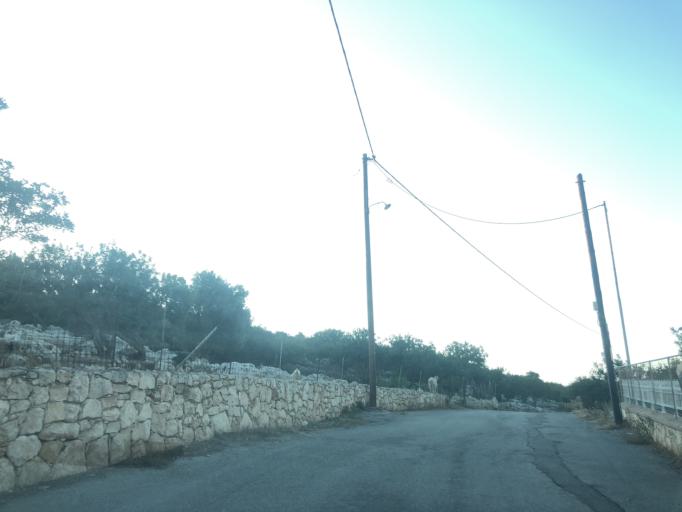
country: GR
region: Crete
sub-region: Nomos Rethymnis
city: Atsipopoulon
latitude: 35.3548
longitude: 24.3975
